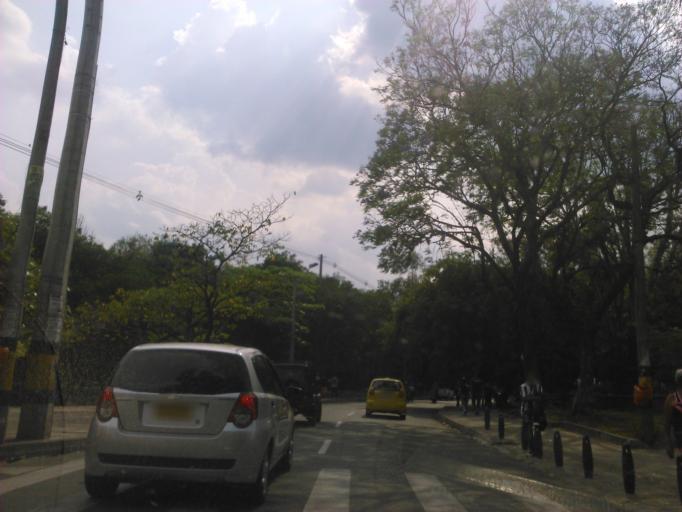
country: CO
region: Antioquia
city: Medellin
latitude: 6.2539
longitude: -75.5890
